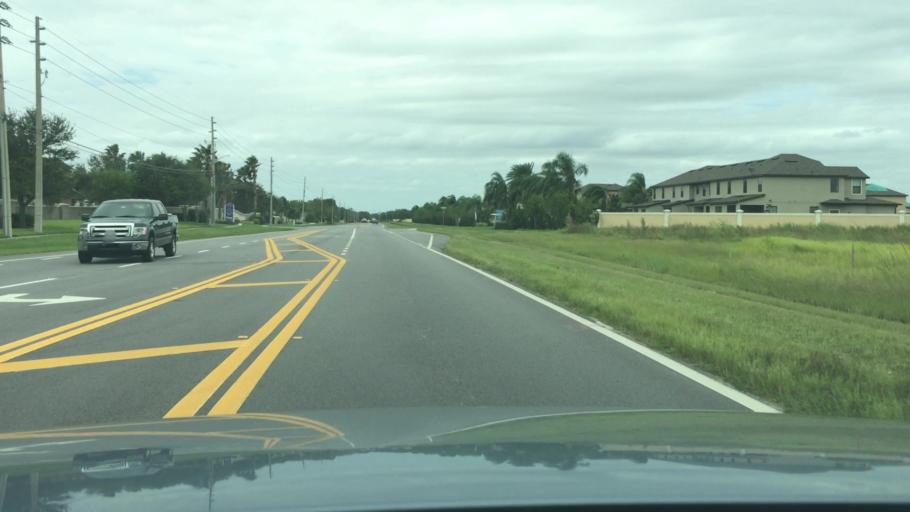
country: US
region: Florida
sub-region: Osceola County
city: Saint Cloud
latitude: 28.1999
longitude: -81.2966
